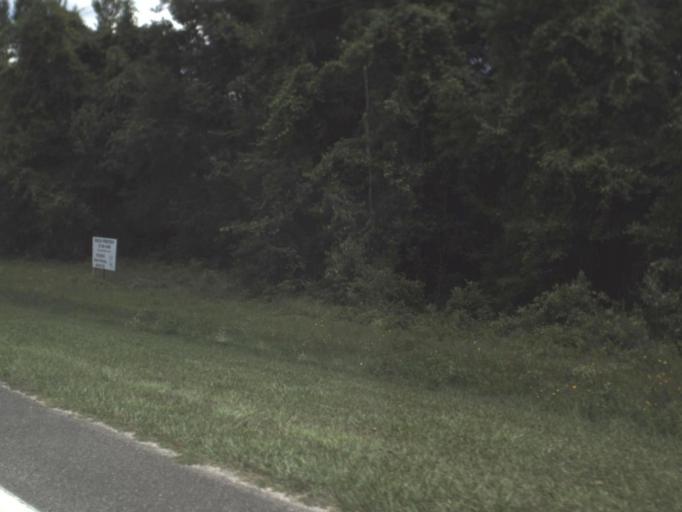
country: US
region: Florida
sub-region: Alachua County
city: High Springs
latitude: 29.9106
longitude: -82.6999
